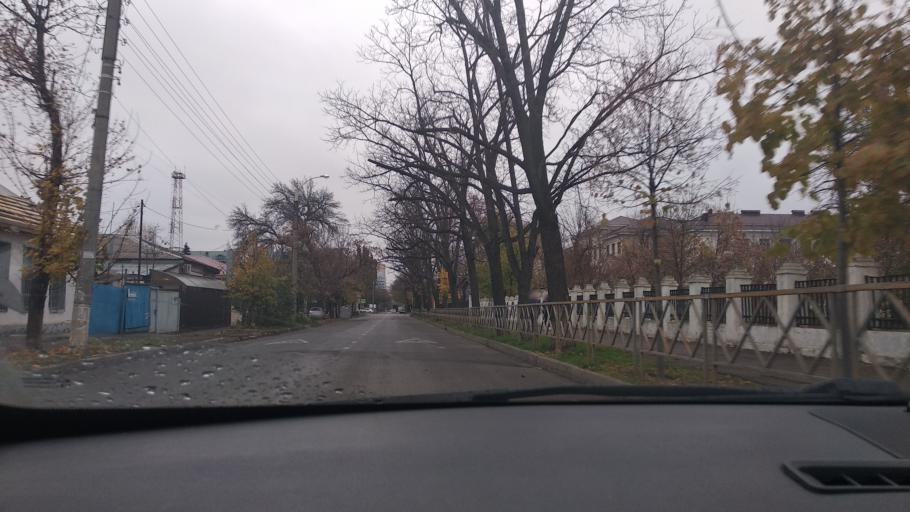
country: RU
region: Krasnodarskiy
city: Krasnodar
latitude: 45.0297
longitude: 38.9834
